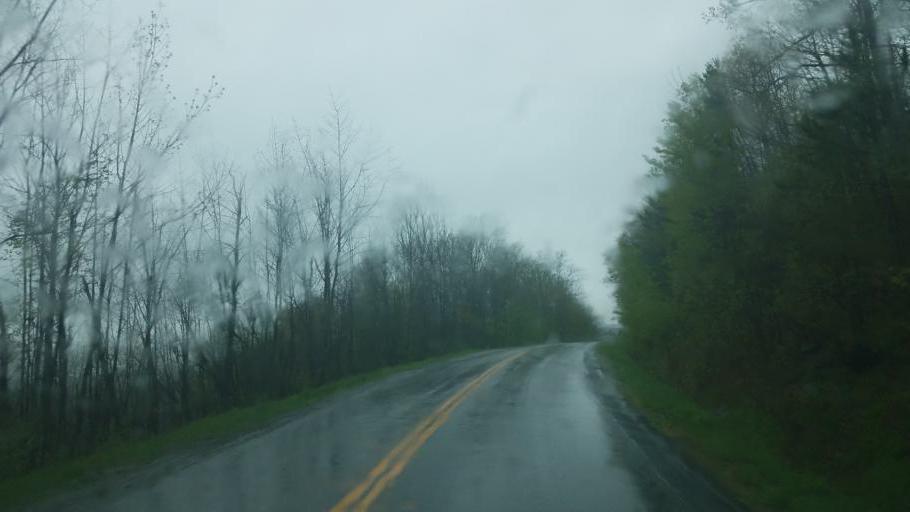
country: US
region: Pennsylvania
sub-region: Tioga County
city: Westfield
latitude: 42.0805
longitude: -77.4745
